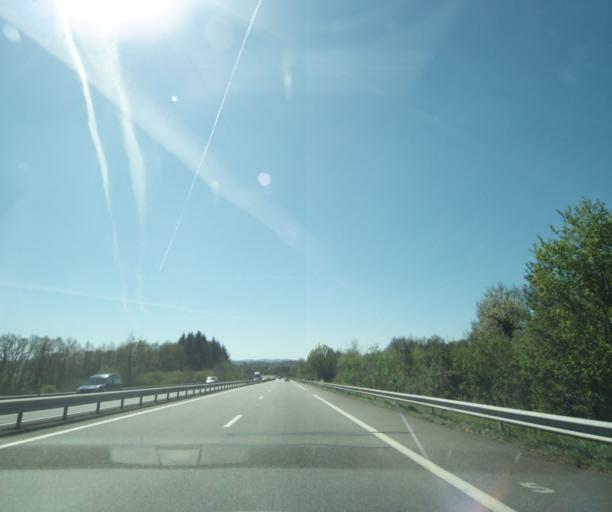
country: FR
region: Limousin
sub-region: Departement de la Creuse
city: Saint-Maurice-la-Souterraine
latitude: 46.1776
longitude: 1.3784
